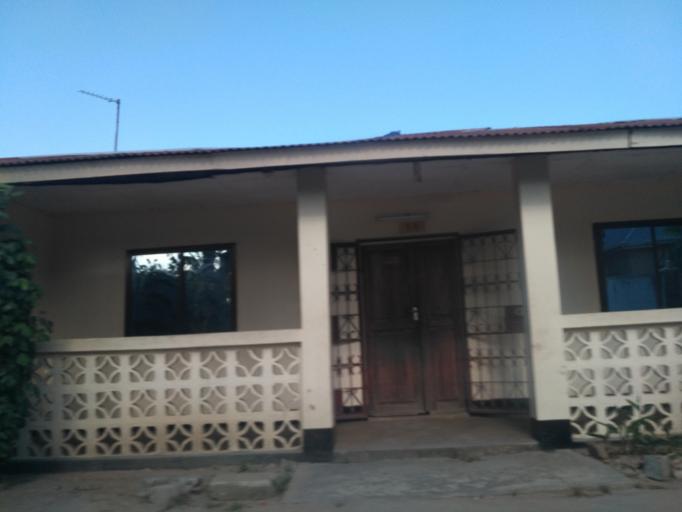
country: TZ
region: Dar es Salaam
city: Magomeni
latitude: -6.7789
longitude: 39.2659
